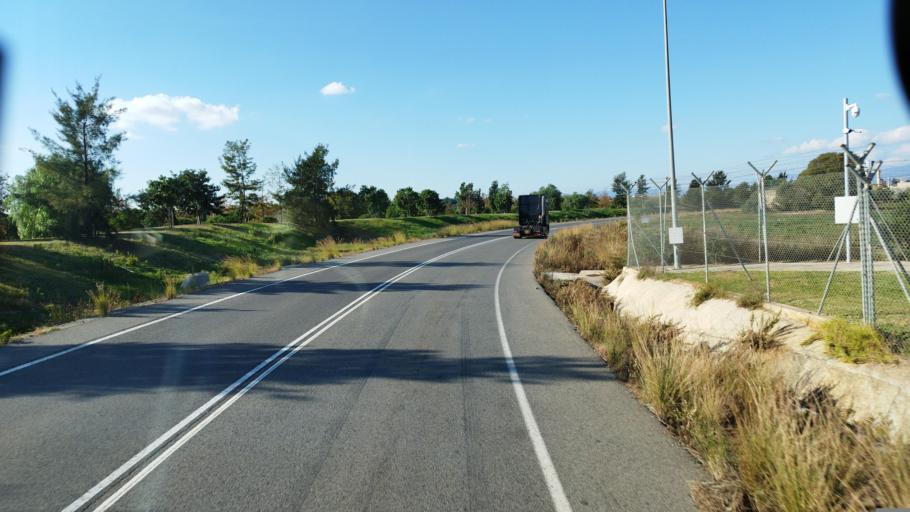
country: ES
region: Catalonia
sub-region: Provincia de Barcelona
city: La Pineda
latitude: 41.0978
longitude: 1.1695
